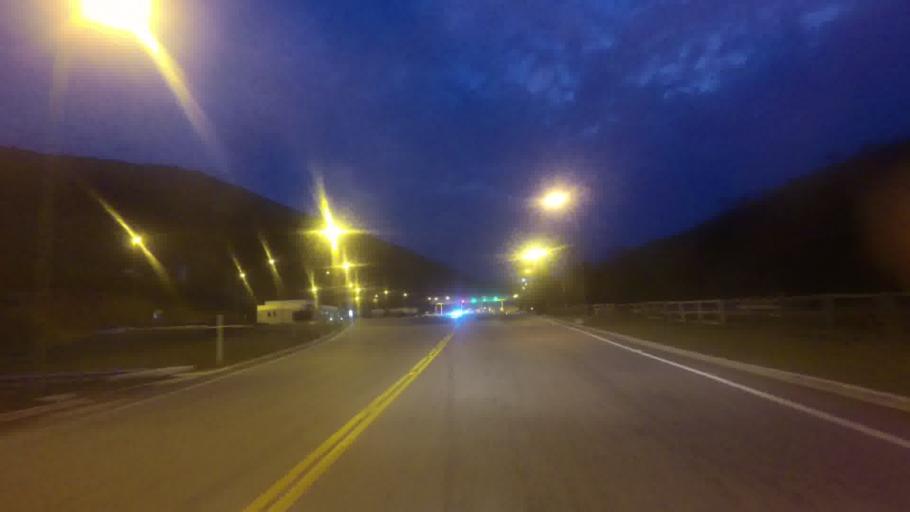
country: BR
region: Rio de Janeiro
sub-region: Sapucaia
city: Sapucaia
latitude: -21.9611
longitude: -42.8604
